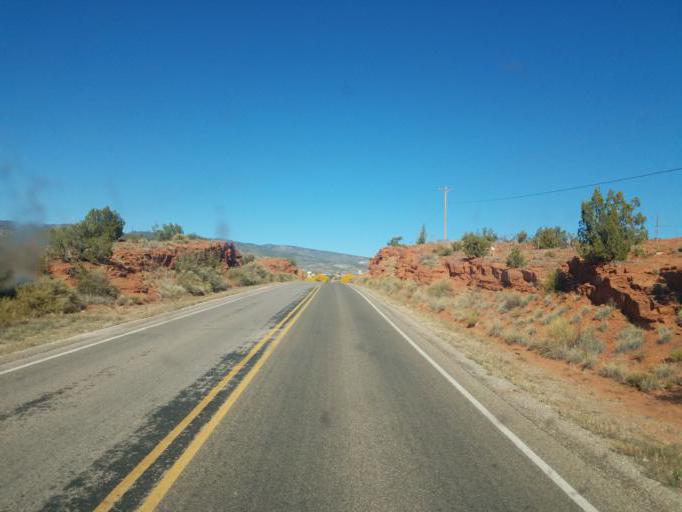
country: US
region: New Mexico
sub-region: Sandoval County
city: Jemez Pueblo
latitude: 35.6470
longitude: -106.7274
